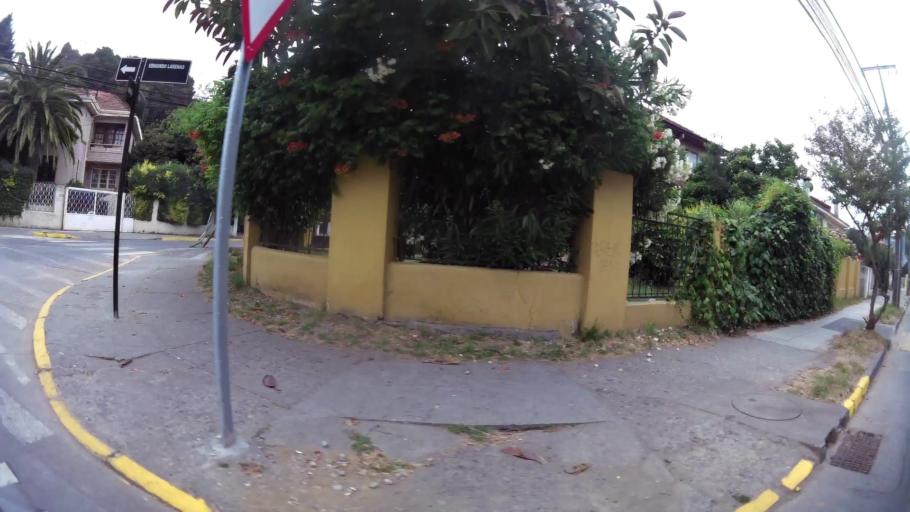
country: CL
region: Biobio
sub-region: Provincia de Concepcion
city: Concepcion
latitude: -36.8317
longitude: -73.0370
